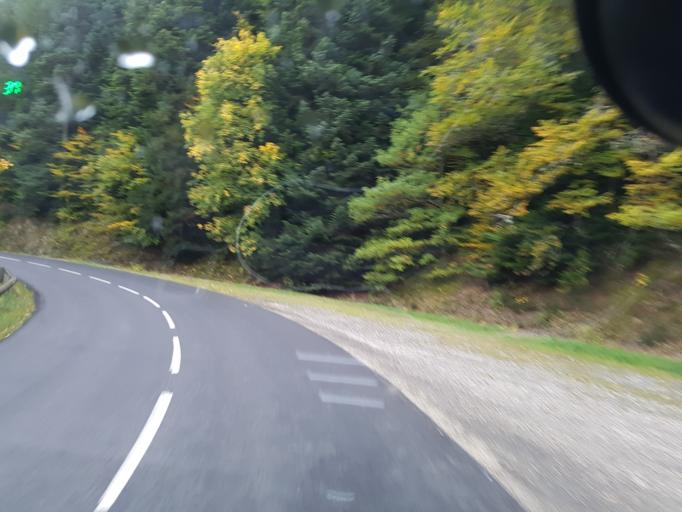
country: FR
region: Auvergne
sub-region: Departement de la Haute-Loire
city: Lapte
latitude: 45.2137
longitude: 4.2044
